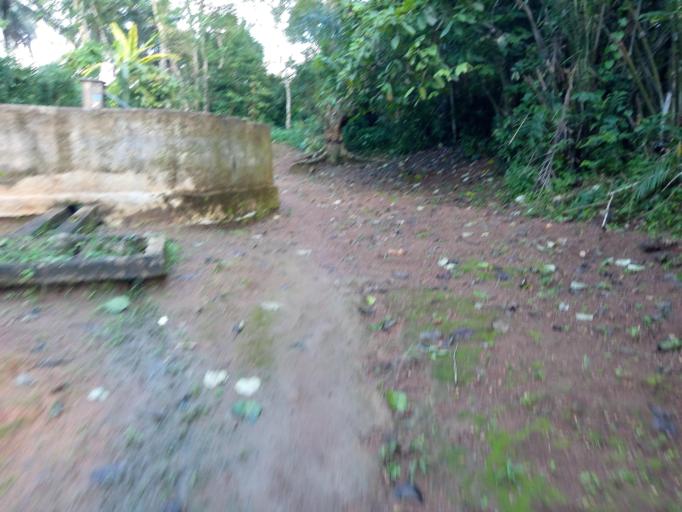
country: SL
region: Eastern Province
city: Buedu
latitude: 8.4788
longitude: -10.3383
